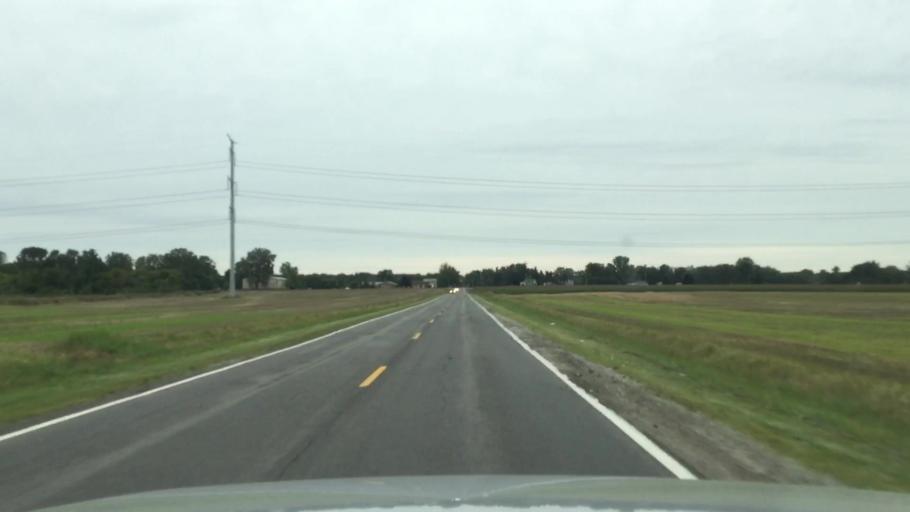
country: US
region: Michigan
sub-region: Washtenaw County
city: Milan
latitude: 42.1180
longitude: -83.6961
